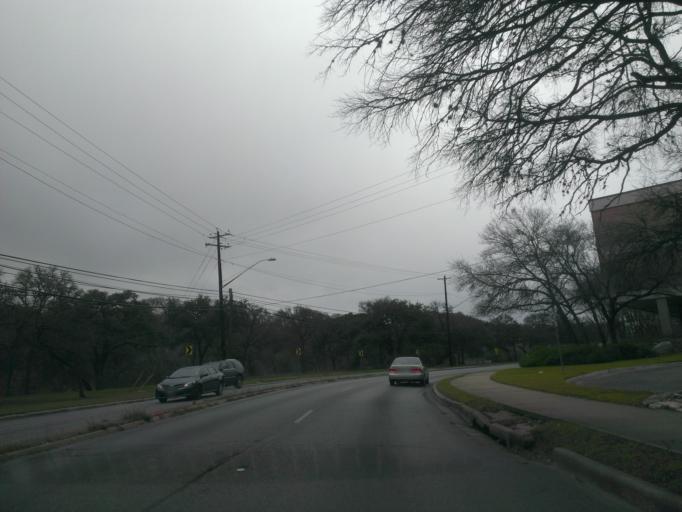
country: US
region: Texas
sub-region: Travis County
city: Austin
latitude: 30.2911
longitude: -97.7510
